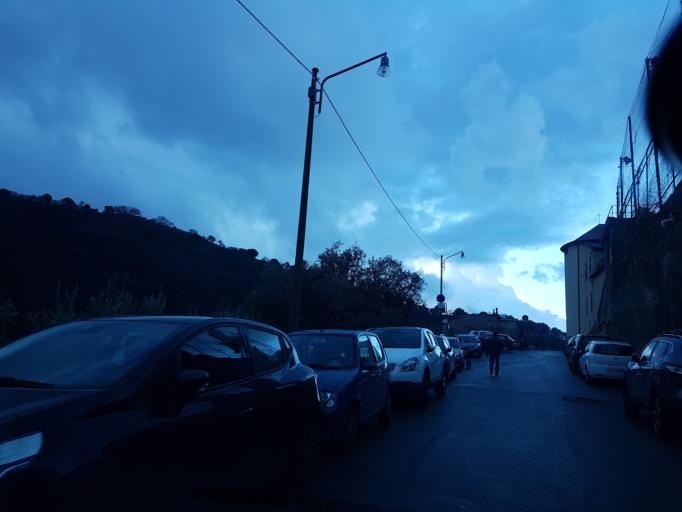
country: IT
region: Liguria
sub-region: Provincia di Genova
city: Genoa
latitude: 44.4315
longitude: 8.9556
